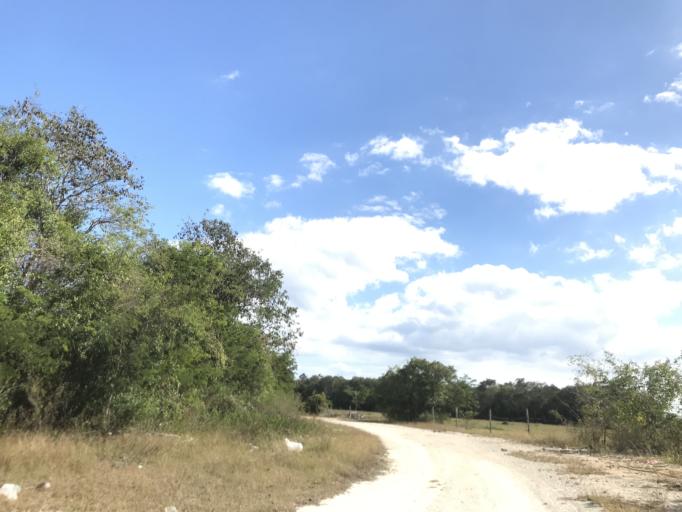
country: CU
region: Cienfuegos
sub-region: Municipio de Aguada de Pasajeros
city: Aguada de Pasajeros
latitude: 22.0761
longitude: -81.0382
